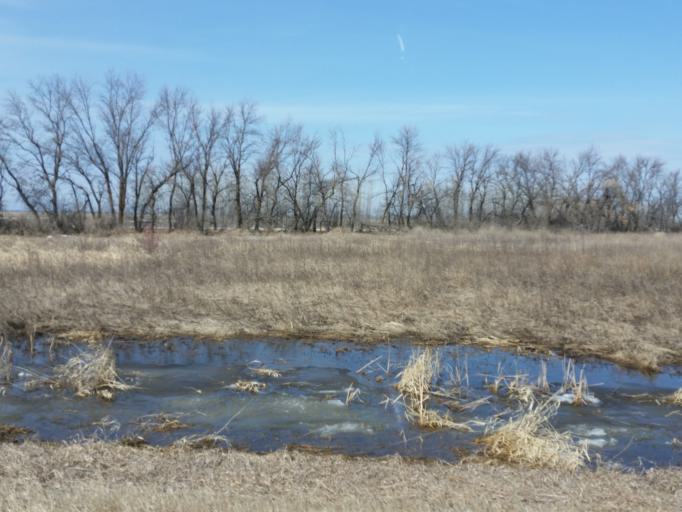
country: US
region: North Dakota
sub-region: Walsh County
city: Grafton
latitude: 48.3249
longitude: -97.1751
